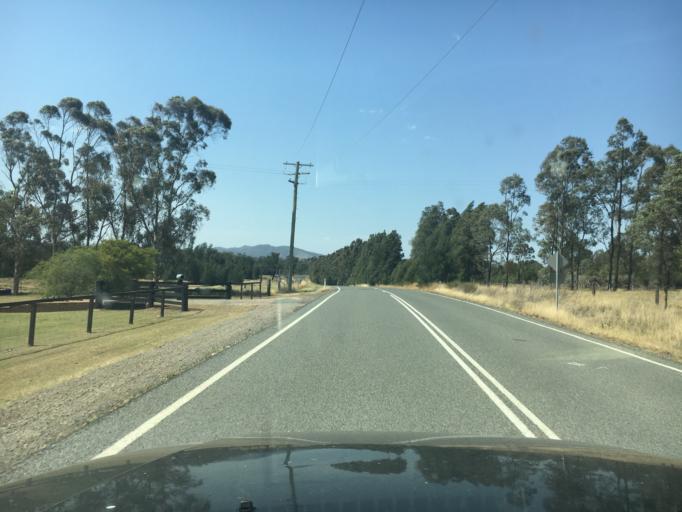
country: AU
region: New South Wales
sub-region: Singleton
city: Singleton
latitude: -32.5477
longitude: 151.2383
